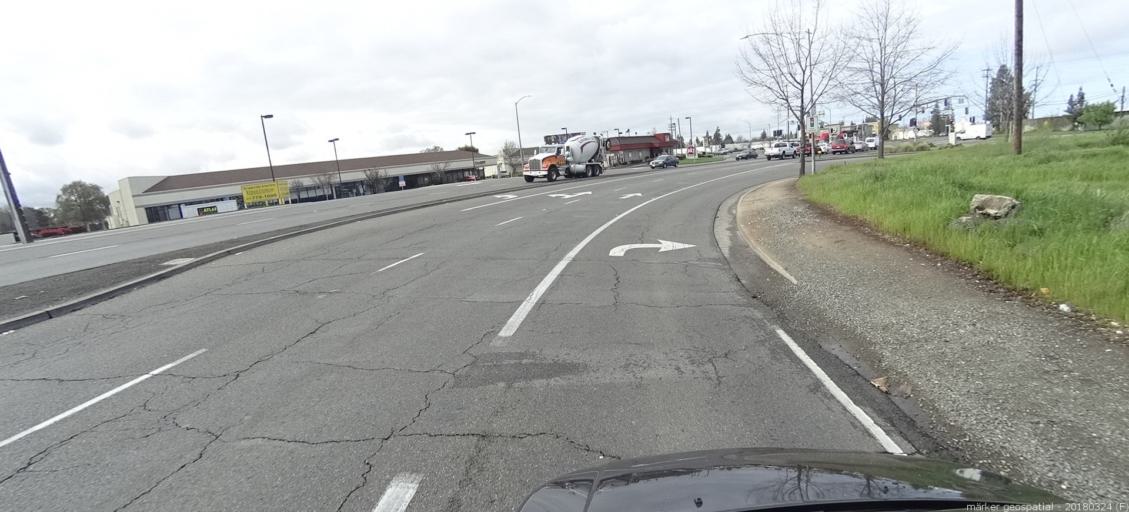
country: US
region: California
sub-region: Sacramento County
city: North Highlands
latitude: 38.6583
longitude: -121.3818
